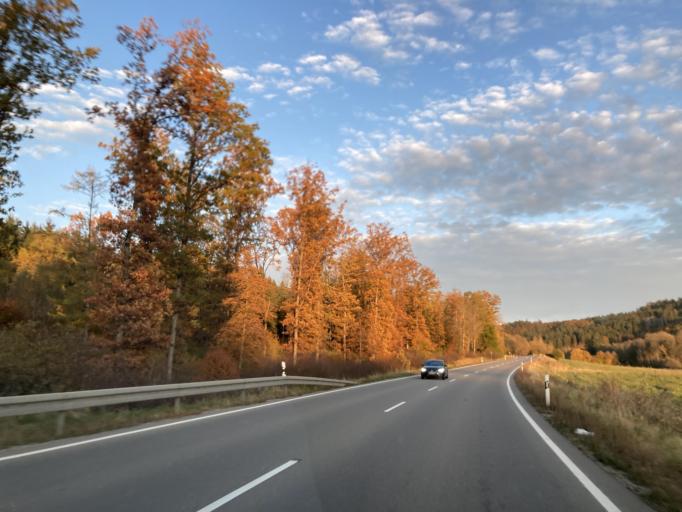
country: DE
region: Baden-Wuerttemberg
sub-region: Freiburg Region
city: Dietingen
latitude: 48.1879
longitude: 8.6701
